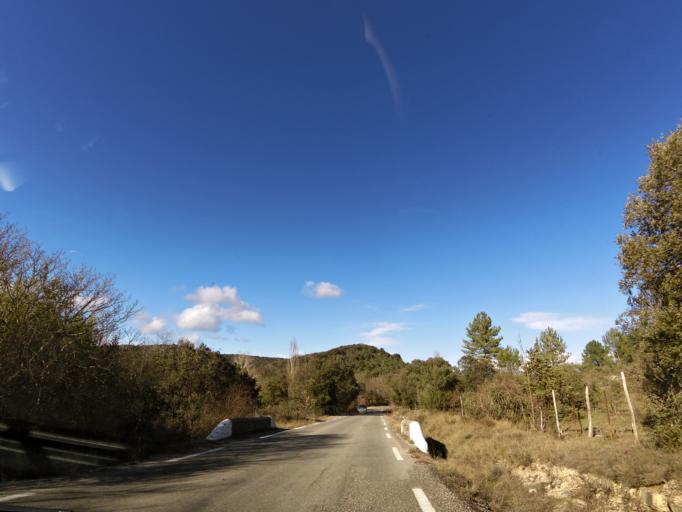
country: FR
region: Languedoc-Roussillon
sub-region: Departement du Gard
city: Sauve
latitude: 43.9684
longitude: 3.9477
